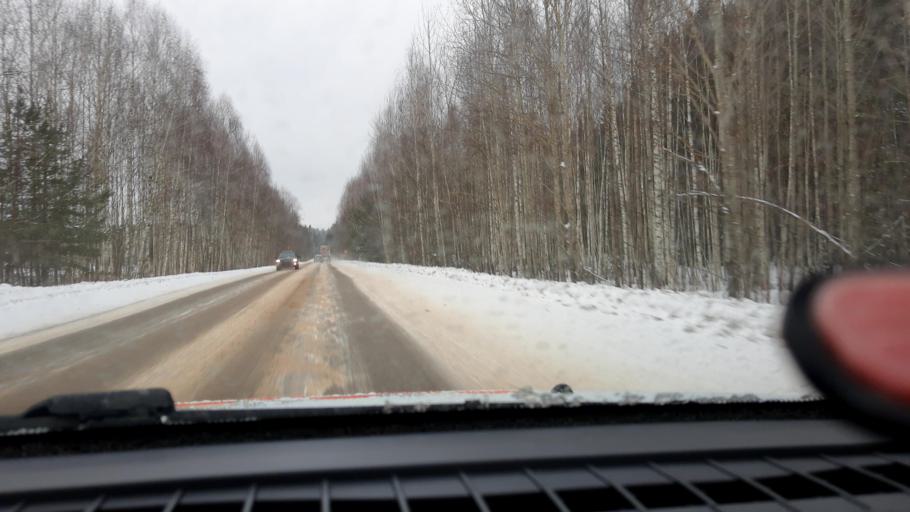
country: RU
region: Nizjnij Novgorod
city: Pamyat' Parizhskoy Kommuny
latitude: 56.2756
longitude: 44.3978
